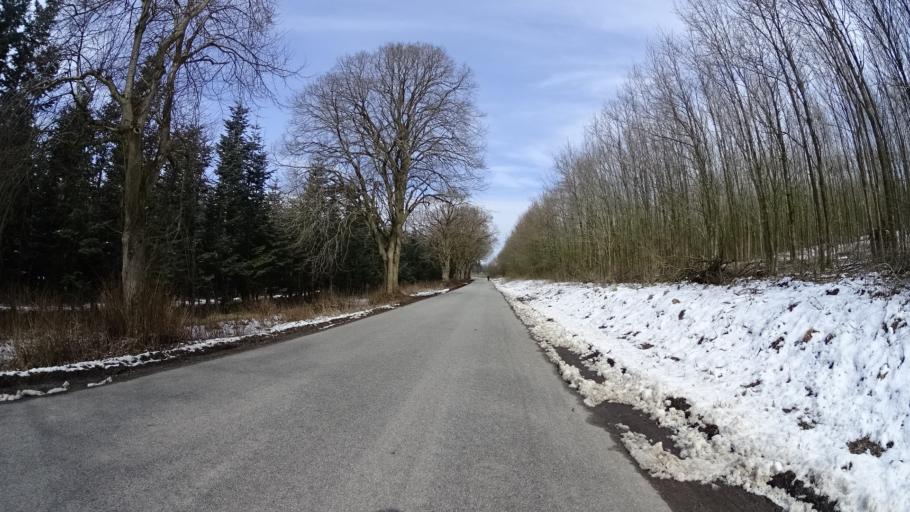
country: DE
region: Schleswig-Holstein
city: Stolpe
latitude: 54.1488
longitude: 10.2327
